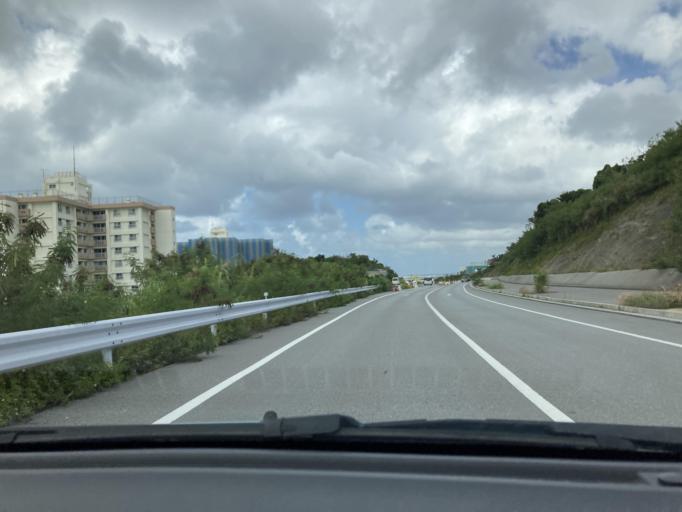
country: JP
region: Okinawa
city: Ginowan
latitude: 26.2653
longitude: 127.7089
